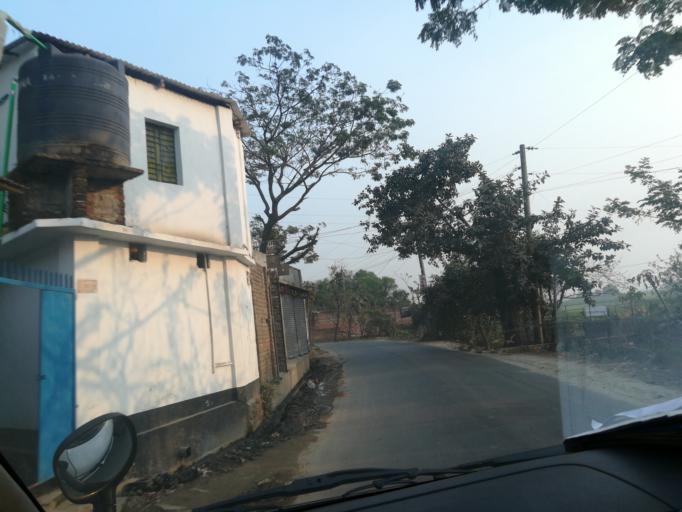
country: BD
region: Dhaka
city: Tungi
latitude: 23.8565
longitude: 90.3282
